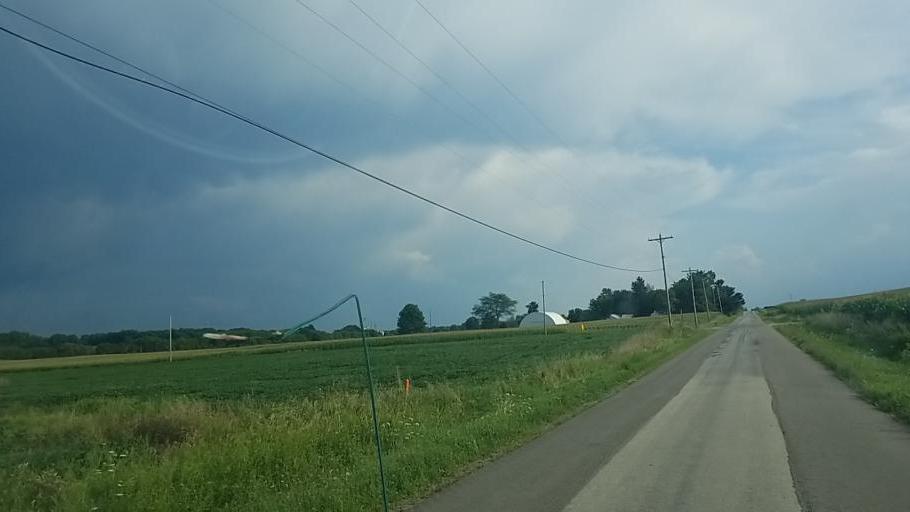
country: US
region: Ohio
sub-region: Wayne County
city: Smithville
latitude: 40.8817
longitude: -81.8613
